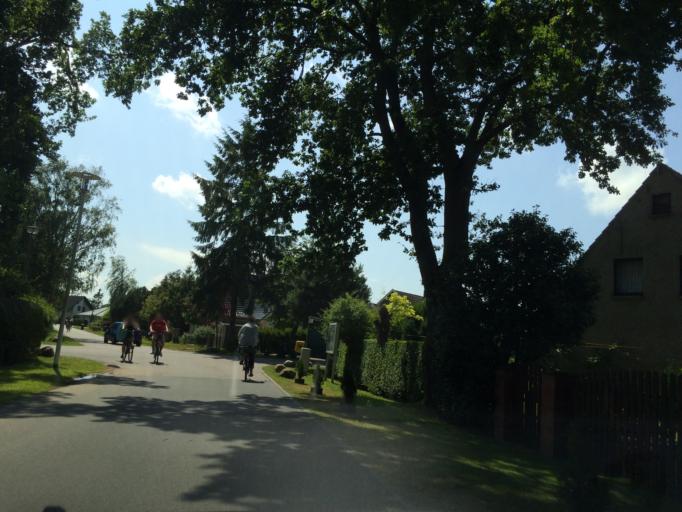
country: DE
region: Mecklenburg-Vorpommern
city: Zingst
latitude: 54.4320
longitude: 12.6797
